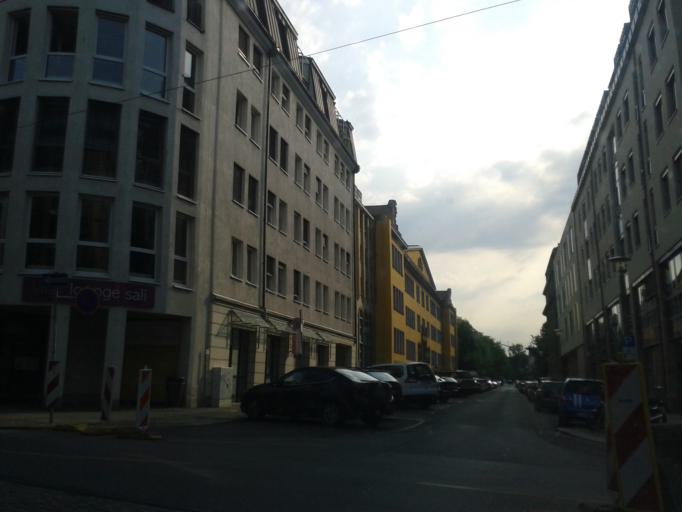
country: DE
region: Saxony
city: Dresden
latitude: 51.0604
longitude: 13.7525
